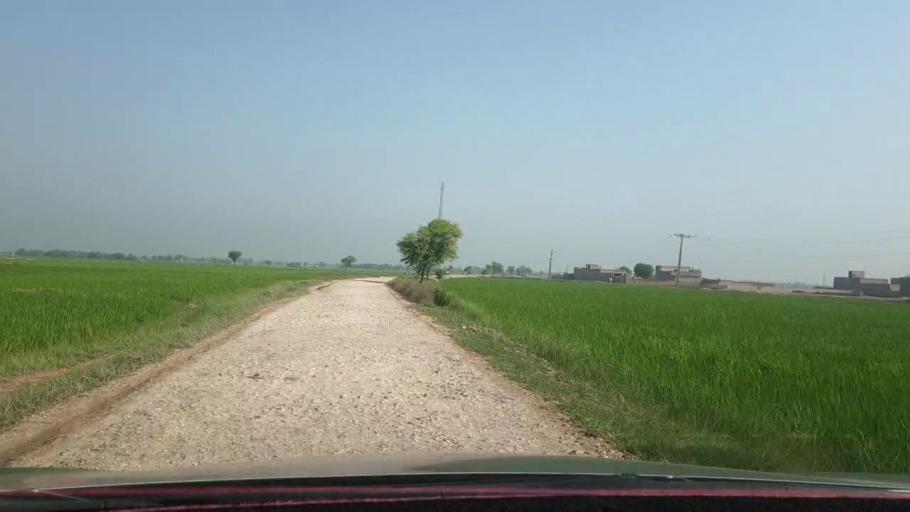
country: PK
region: Sindh
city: Nasirabad
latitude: 27.4833
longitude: 67.9256
